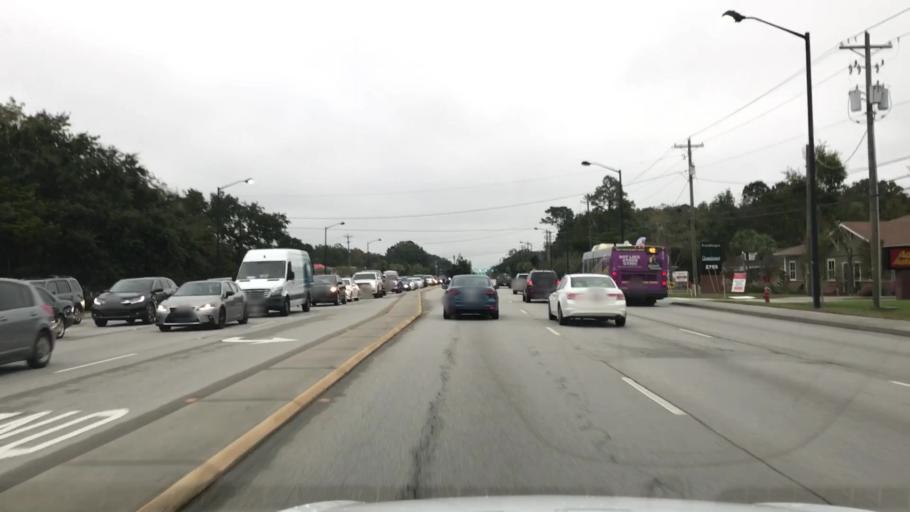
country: US
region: South Carolina
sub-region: Charleston County
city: Isle of Palms
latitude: 32.8560
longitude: -79.7995
